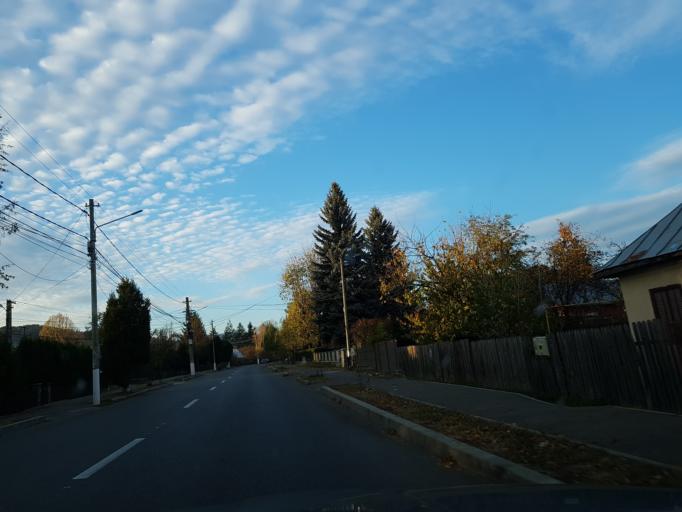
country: RO
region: Prahova
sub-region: Oras Breaza
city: Breaza de Sus
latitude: 45.1924
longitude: 25.6581
